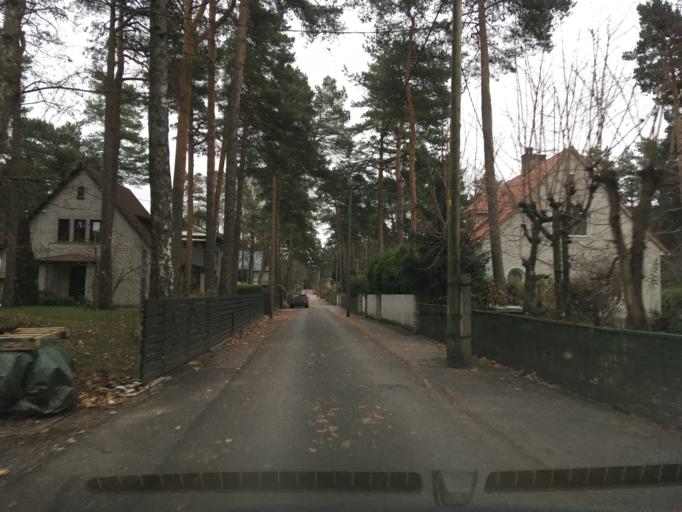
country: EE
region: Harju
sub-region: Saue vald
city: Laagri
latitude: 59.3823
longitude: 24.6850
